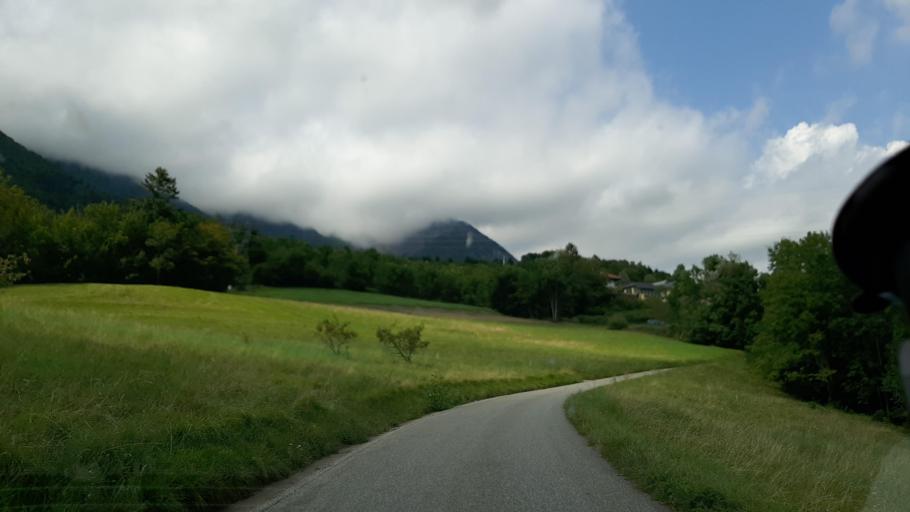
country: FR
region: Rhone-Alpes
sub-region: Departement de la Savoie
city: Mercury
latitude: 45.6927
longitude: 6.3618
